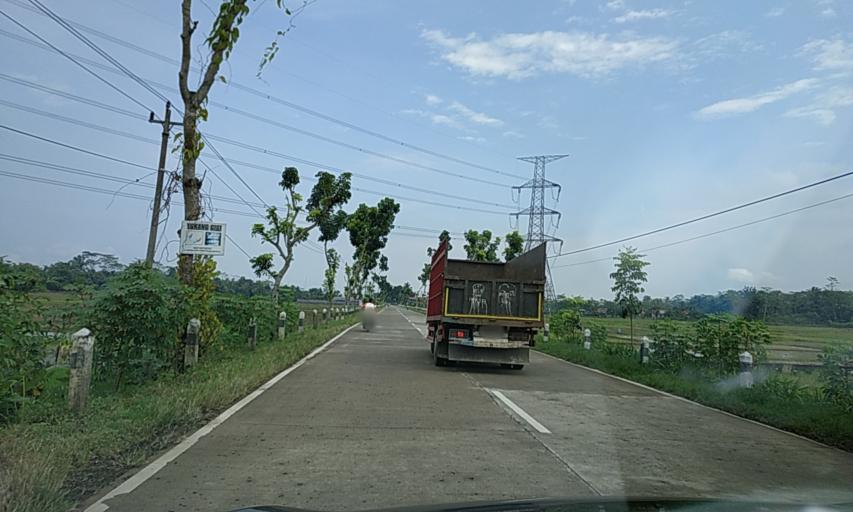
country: ID
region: Central Java
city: Tambangan
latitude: -7.4830
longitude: 108.8300
